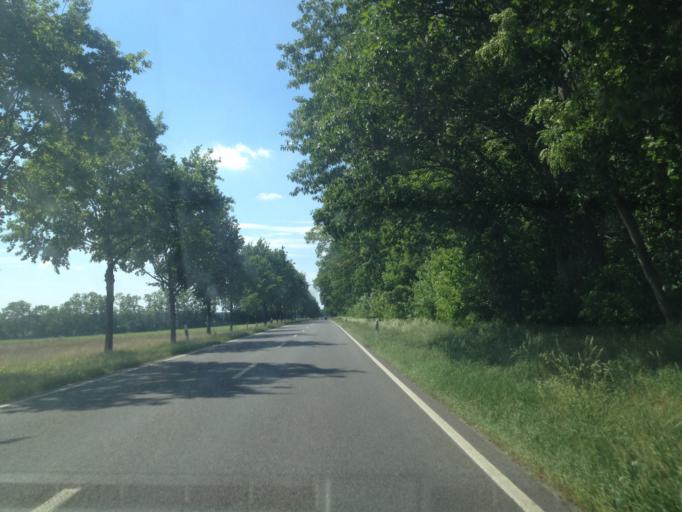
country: DE
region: Brandenburg
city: Marienwerder
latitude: 52.8525
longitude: 13.5746
